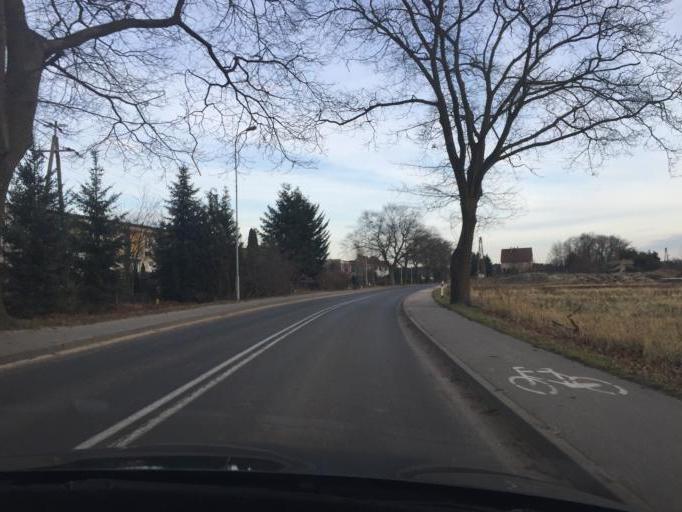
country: PL
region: Lubusz
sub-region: Powiat zarski
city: Brody
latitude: 51.7875
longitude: 14.7825
